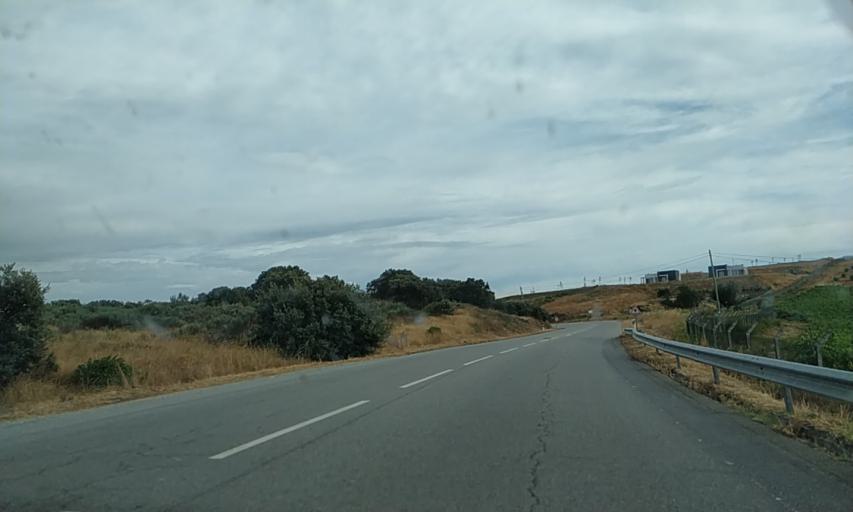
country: PT
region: Viseu
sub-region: Sao Joao da Pesqueira
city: Sao Joao da Pesqueira
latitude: 41.1212
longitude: -7.3901
